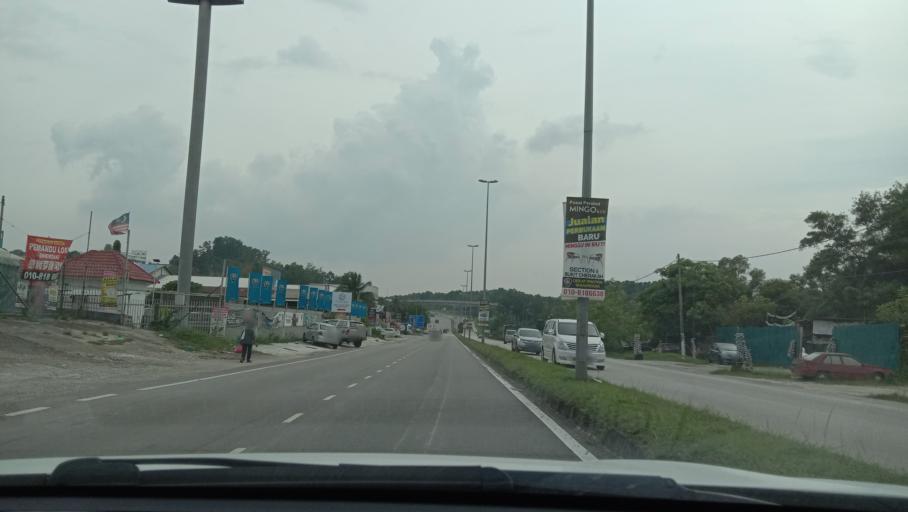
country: MY
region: Selangor
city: Kampung Baru Subang
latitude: 3.1339
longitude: 101.5259
